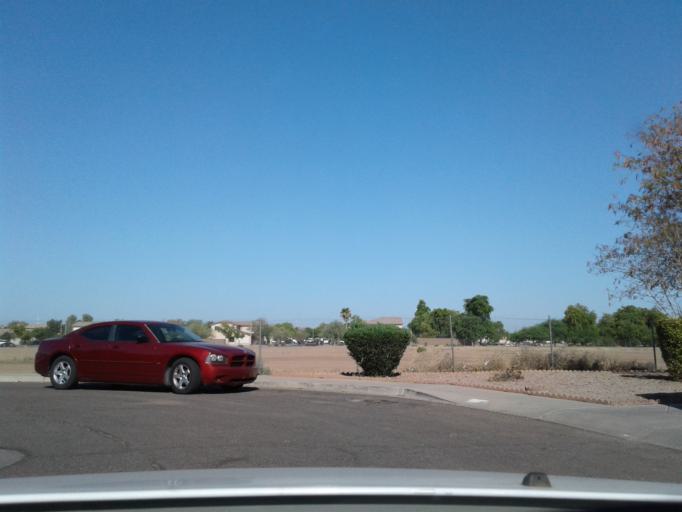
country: US
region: Arizona
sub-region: Maricopa County
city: Laveen
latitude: 33.4120
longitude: -112.1907
